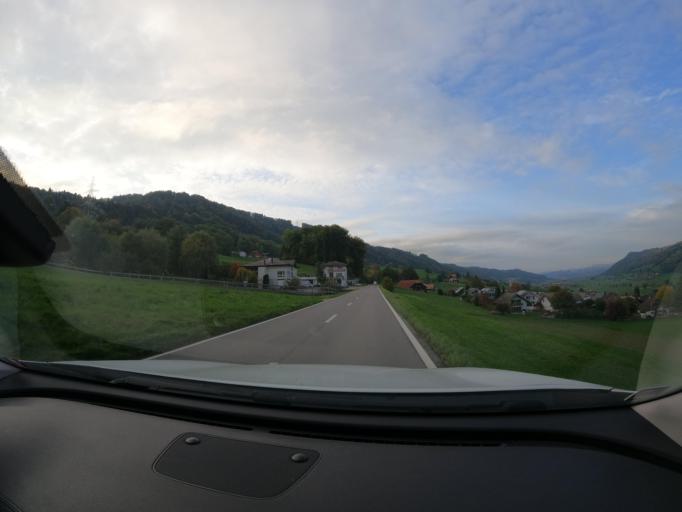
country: CH
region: Bern
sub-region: Bern-Mittelland District
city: Hermiswil
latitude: 46.8350
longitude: 7.4954
